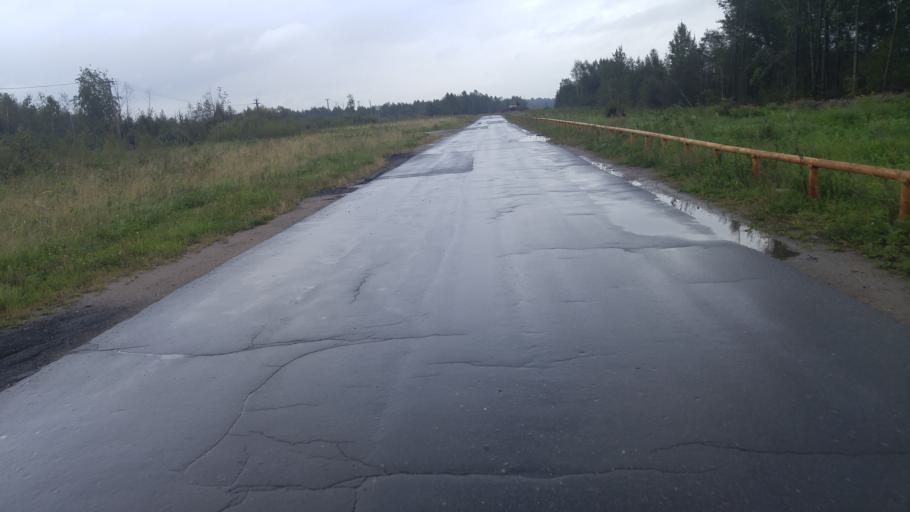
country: RU
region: St.-Petersburg
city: Ust'-Izhora
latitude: 59.7829
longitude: 30.5729
